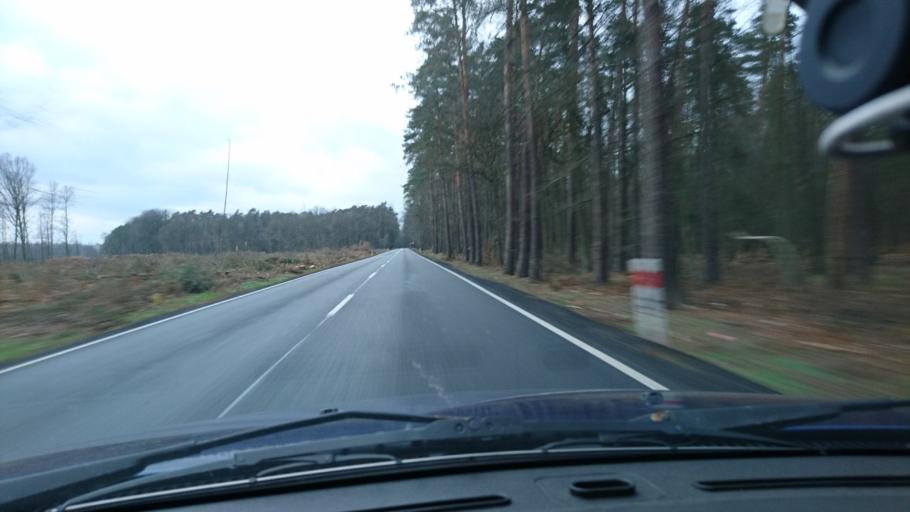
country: PL
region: Opole Voivodeship
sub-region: Powiat kluczborski
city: Kluczbork
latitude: 50.9406
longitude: 18.3260
